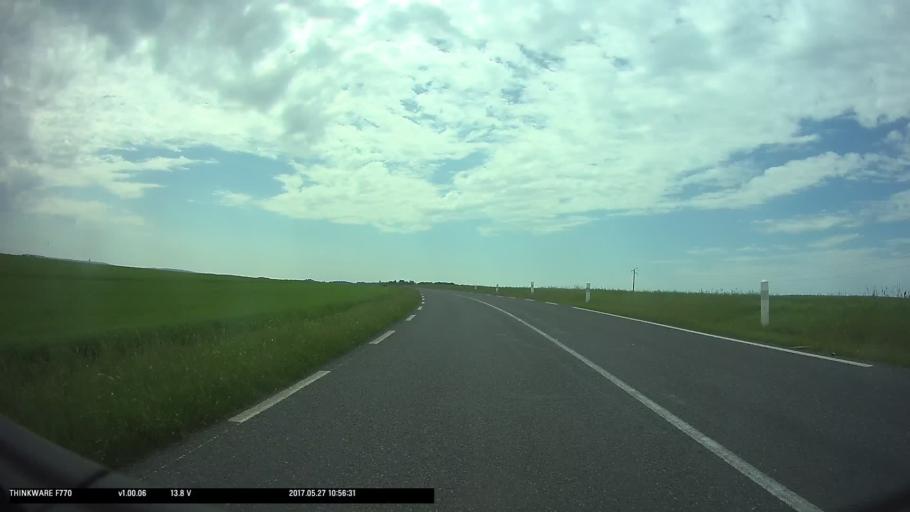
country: FR
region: Picardie
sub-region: Departement de l'Oise
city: Chaumont-en-Vexin
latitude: 49.2429
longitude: 1.8747
